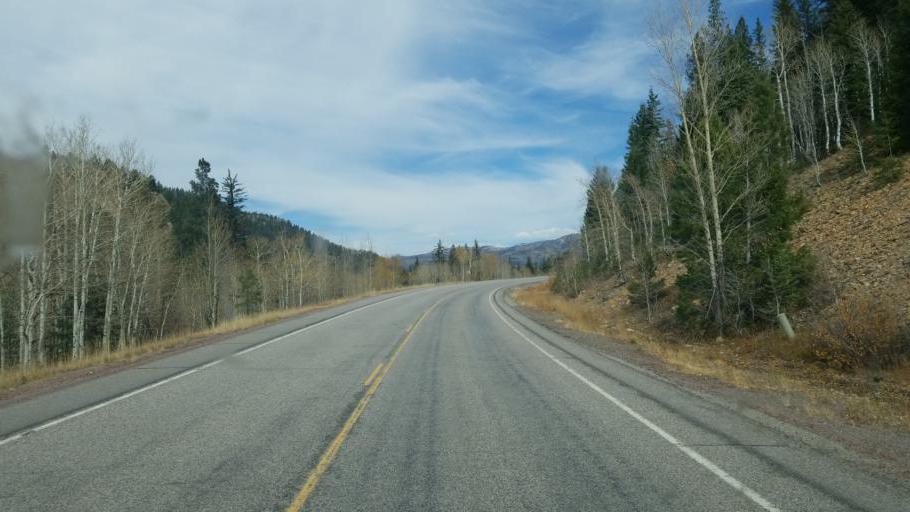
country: US
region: New Mexico
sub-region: Rio Arriba County
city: Chama
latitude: 36.9409
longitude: -106.5492
